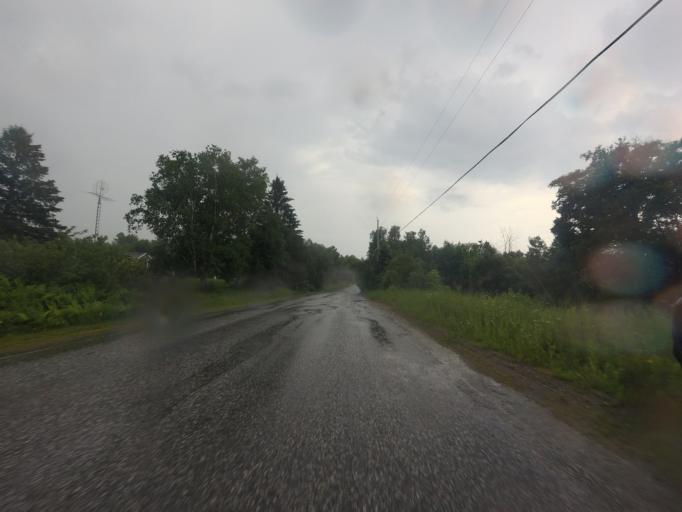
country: CA
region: Quebec
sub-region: Outaouais
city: Maniwaki
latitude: 46.4100
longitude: -75.9579
